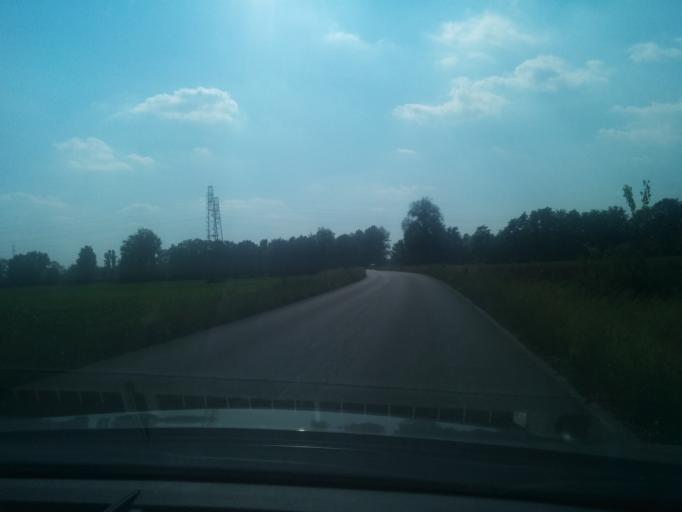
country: IT
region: Friuli Venezia Giulia
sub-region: Provincia di Udine
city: Reana del Rojale
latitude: 46.1288
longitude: 13.2494
